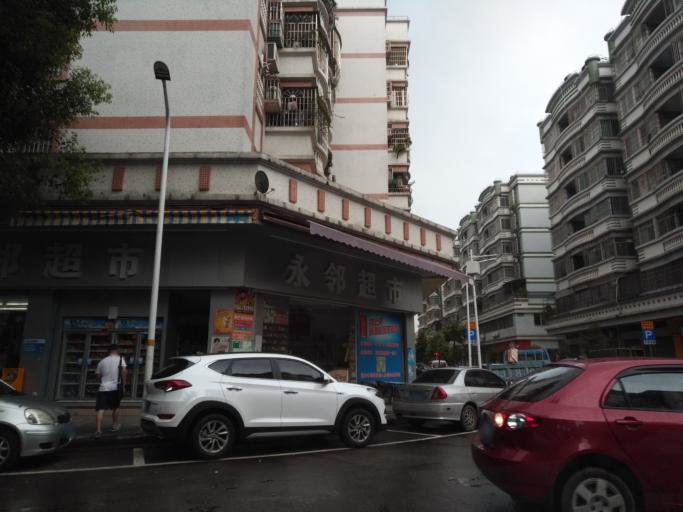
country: CN
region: Guangdong
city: Jianghai
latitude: 22.5719
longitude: 113.1075
